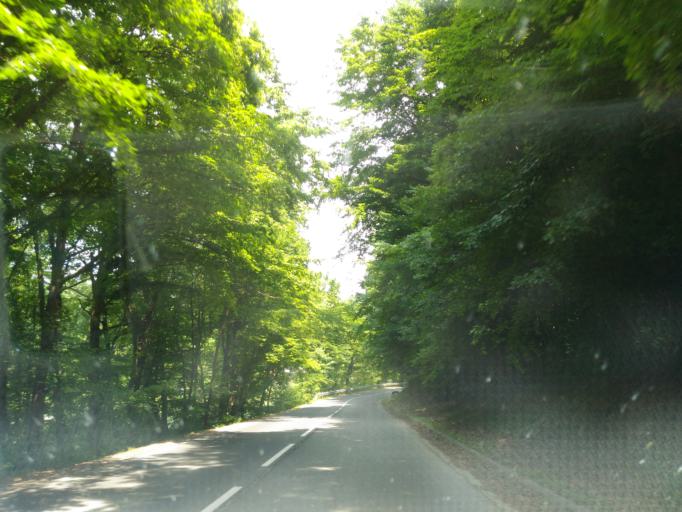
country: HU
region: Baranya
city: Komlo
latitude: 46.1806
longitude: 18.2101
